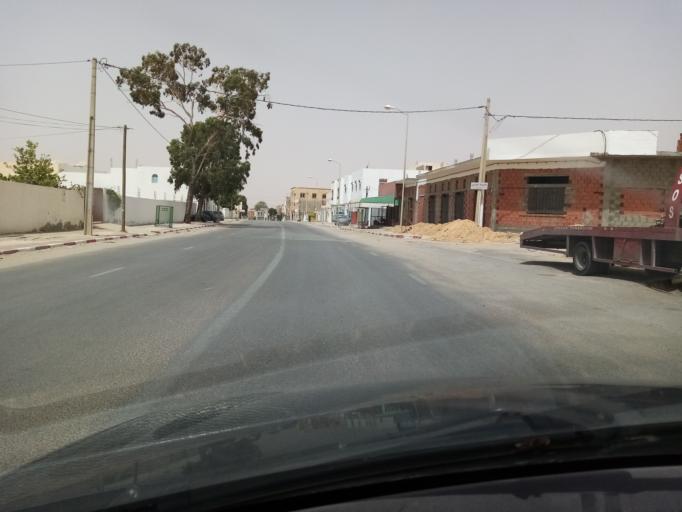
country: TN
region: Tataouine
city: Tataouine
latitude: 32.9198
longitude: 10.4346
